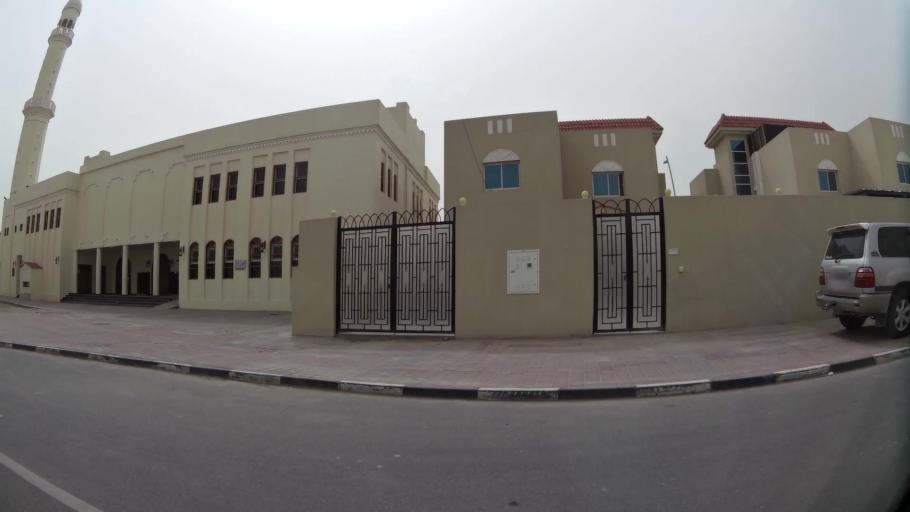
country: QA
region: Baladiyat ad Dawhah
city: Doha
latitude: 25.2304
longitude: 51.5357
